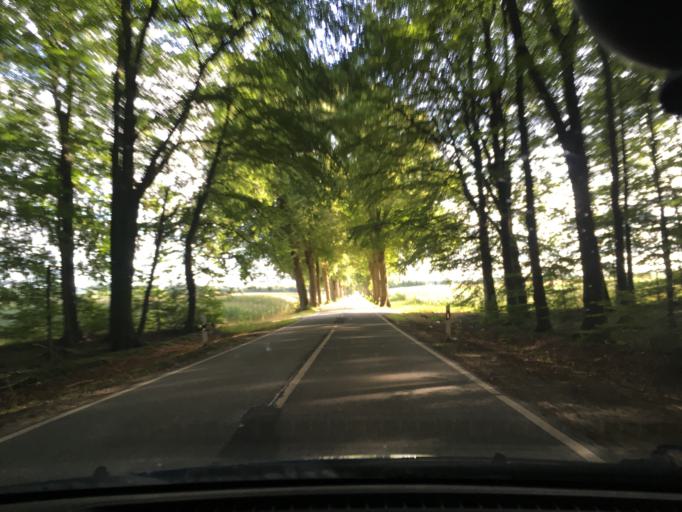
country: DE
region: Lower Saxony
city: Brackel
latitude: 53.3149
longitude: 10.0585
